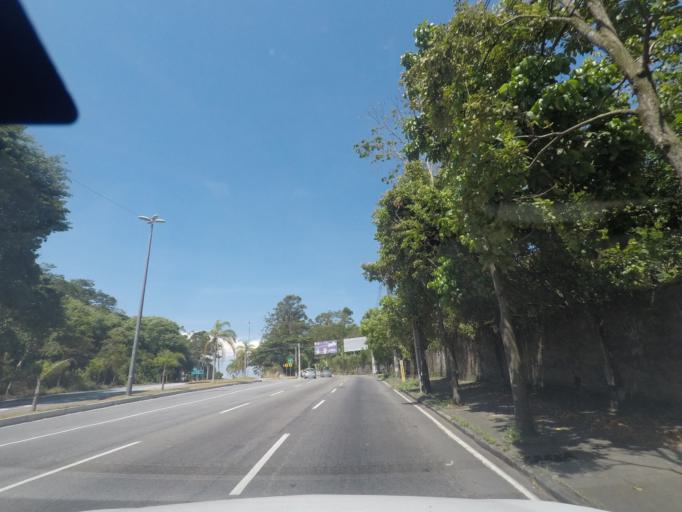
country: BR
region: Rio de Janeiro
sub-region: Niteroi
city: Niteroi
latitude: -22.9216
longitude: -43.0547
